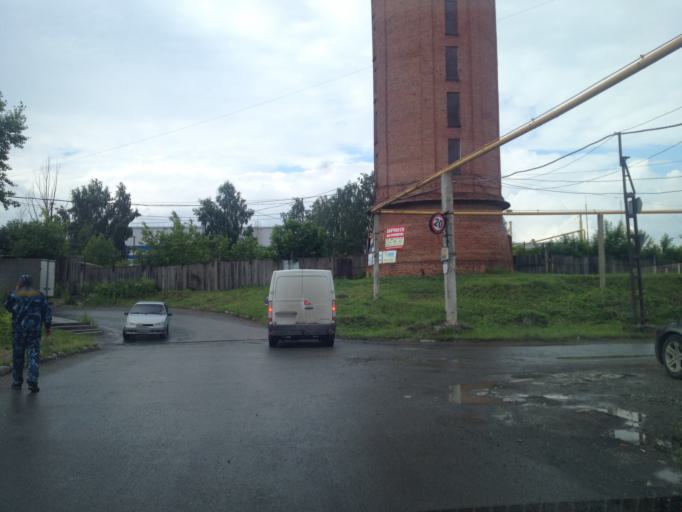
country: RU
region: Sverdlovsk
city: Yekaterinburg
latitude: 56.9114
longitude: 60.6334
